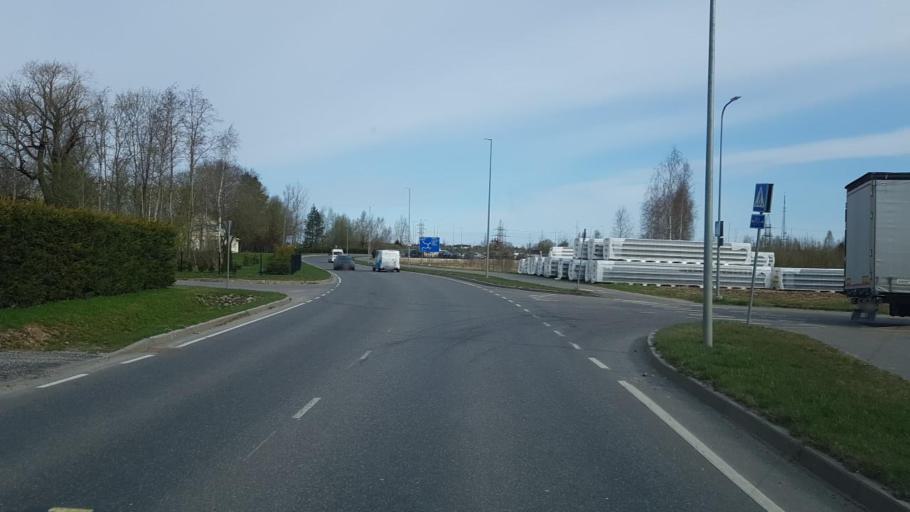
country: EE
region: Tartu
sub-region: UElenurme vald
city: Ulenurme
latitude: 58.3426
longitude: 26.7007
